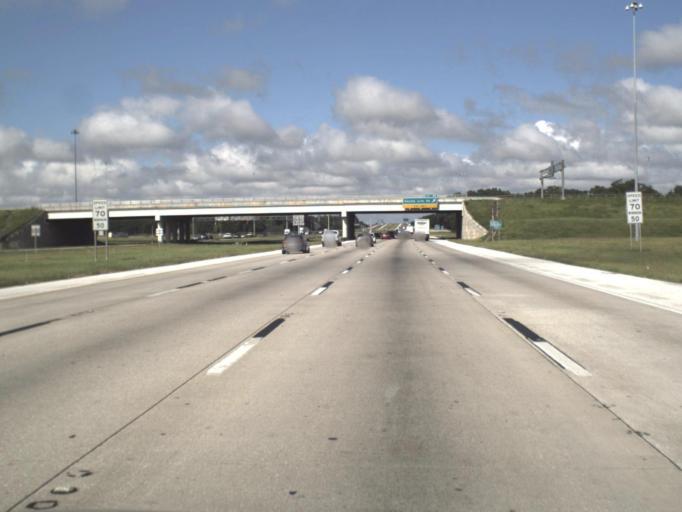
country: US
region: Florida
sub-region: Polk County
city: Winston
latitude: 28.0369
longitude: -82.0536
